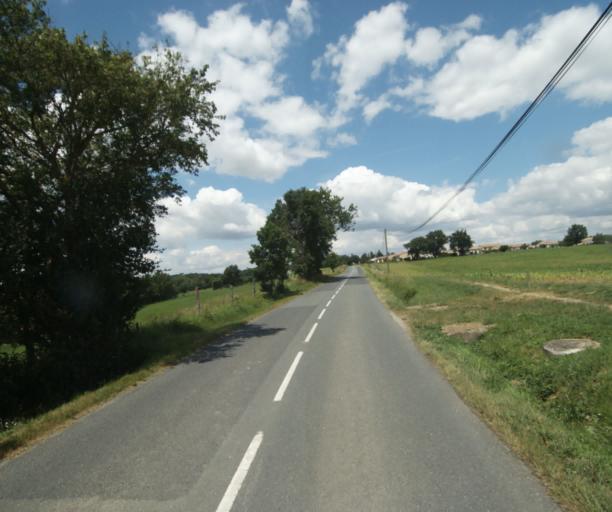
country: FR
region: Midi-Pyrenees
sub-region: Departement du Tarn
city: Soual
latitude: 43.5315
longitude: 2.0619
